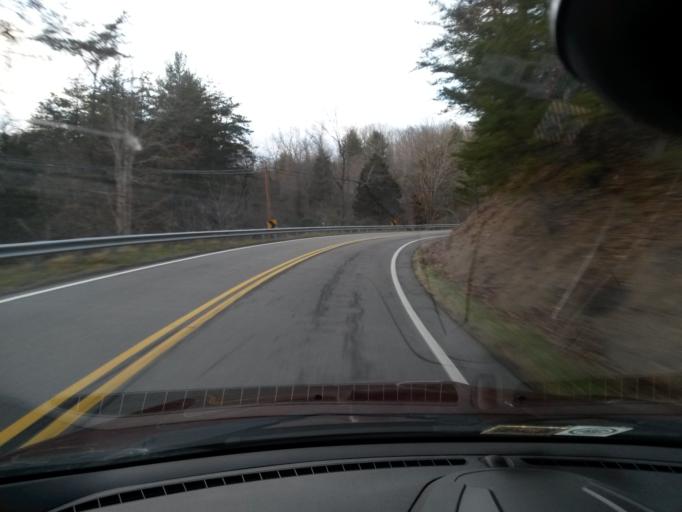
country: US
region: Virginia
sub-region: City of Covington
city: Covington
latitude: 37.8007
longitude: -80.0769
